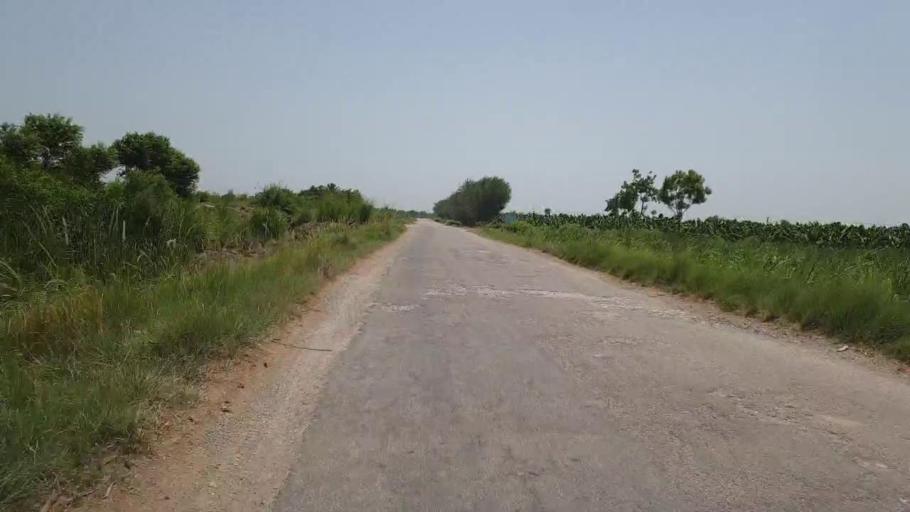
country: PK
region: Sindh
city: Daur
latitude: 26.3844
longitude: 68.1789
